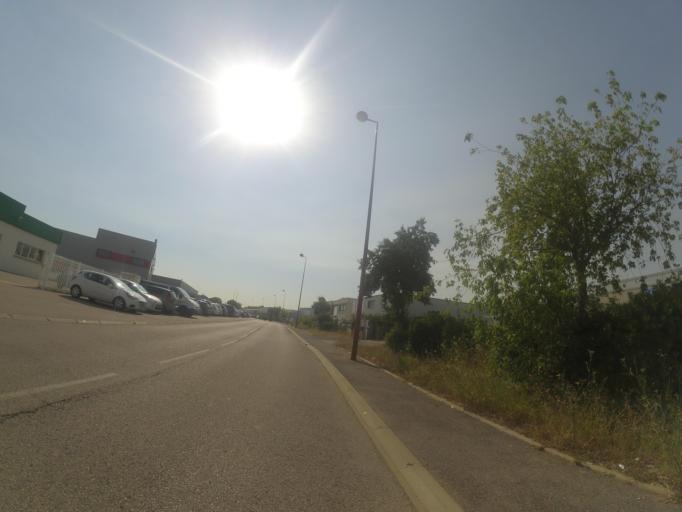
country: FR
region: Languedoc-Roussillon
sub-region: Departement des Pyrenees-Orientales
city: Toulouges
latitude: 42.6624
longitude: 2.8219
